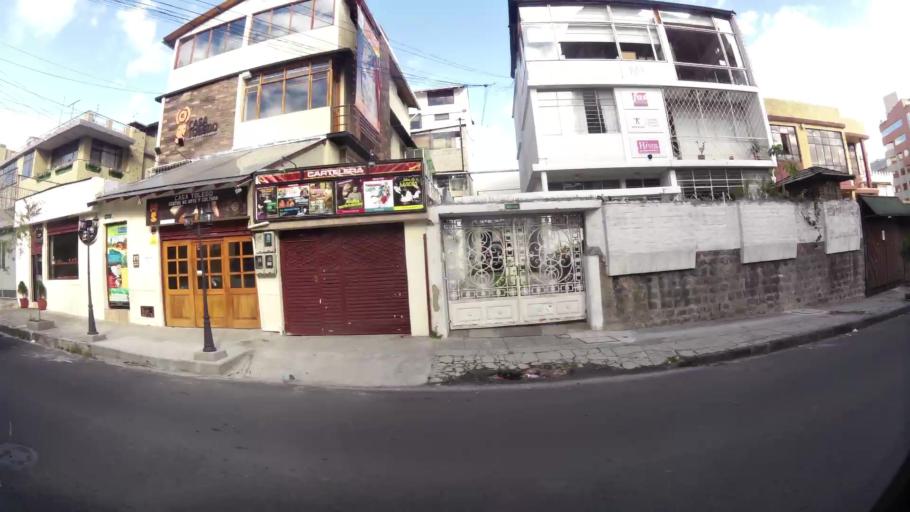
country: EC
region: Pichincha
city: Quito
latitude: -0.2051
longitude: -78.4820
